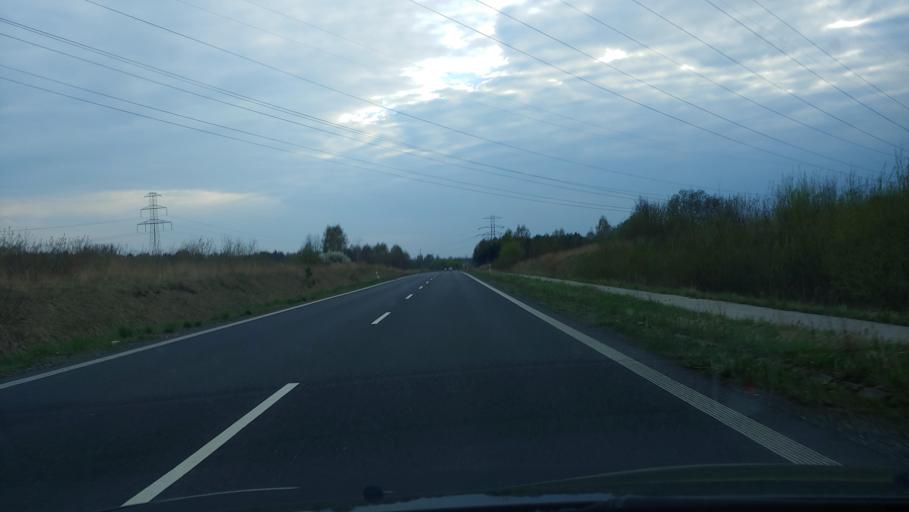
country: PL
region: Silesian Voivodeship
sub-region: Jaworzno
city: Jaworzno
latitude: 50.1630
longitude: 19.2789
